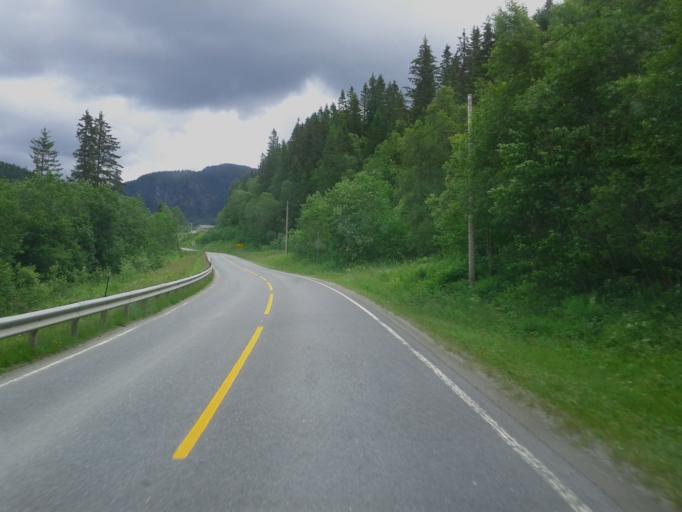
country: NO
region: Sor-Trondelag
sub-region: Midtre Gauldal
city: Storen
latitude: 62.9421
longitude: 10.6411
